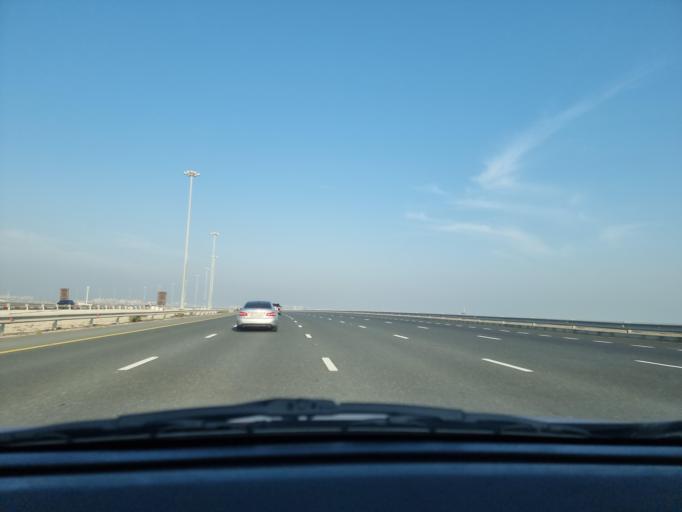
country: AE
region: Abu Dhabi
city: Abu Dhabi
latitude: 24.5421
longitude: 54.4824
